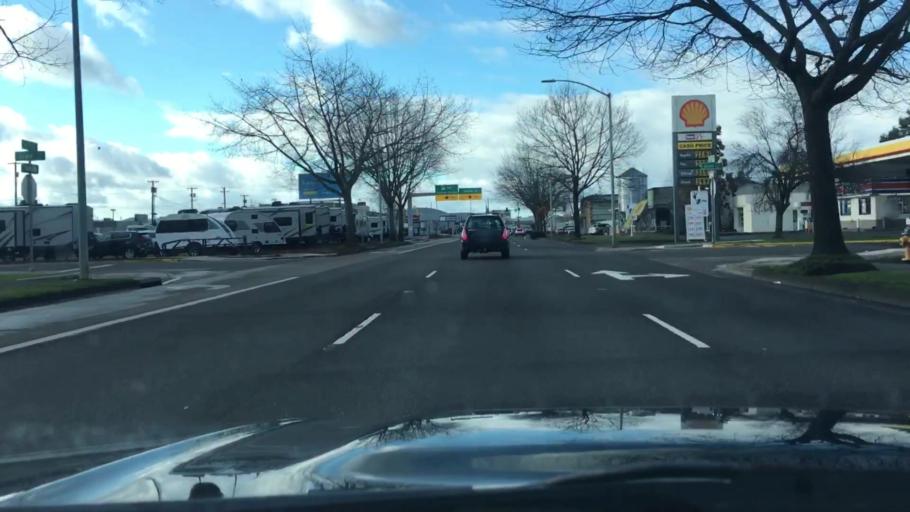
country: US
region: Oregon
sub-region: Lane County
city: Eugene
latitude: 44.0533
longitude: -123.1198
